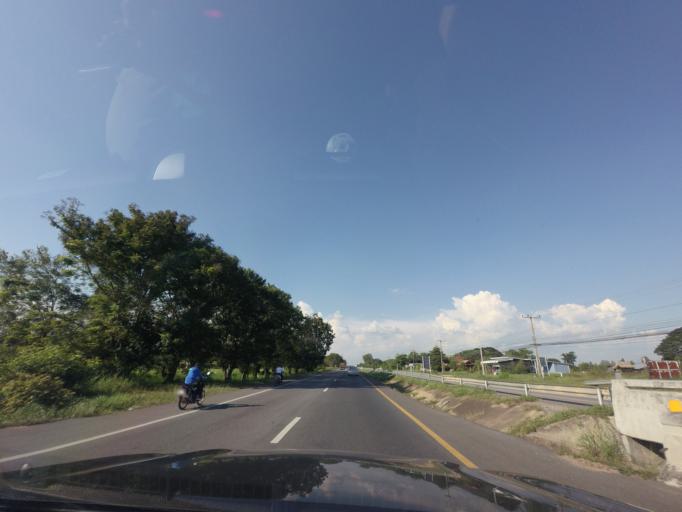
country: TH
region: Khon Kaen
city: Non Sila
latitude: 15.9710
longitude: 102.6928
